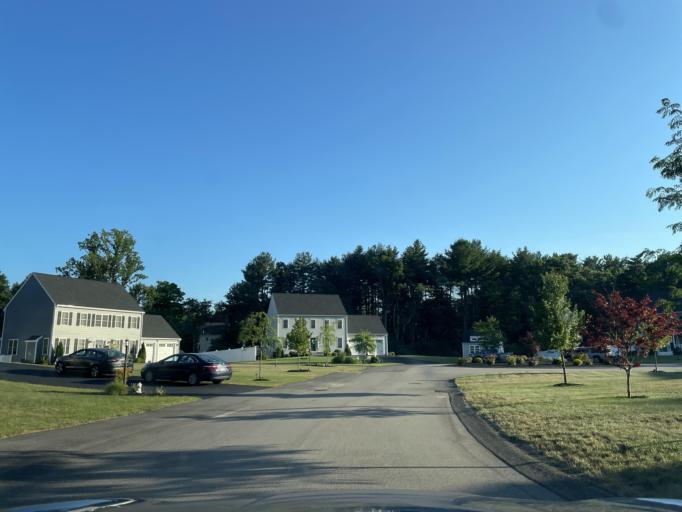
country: US
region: Massachusetts
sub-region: Plymouth County
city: East Bridgewater
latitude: 42.0144
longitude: -70.9646
